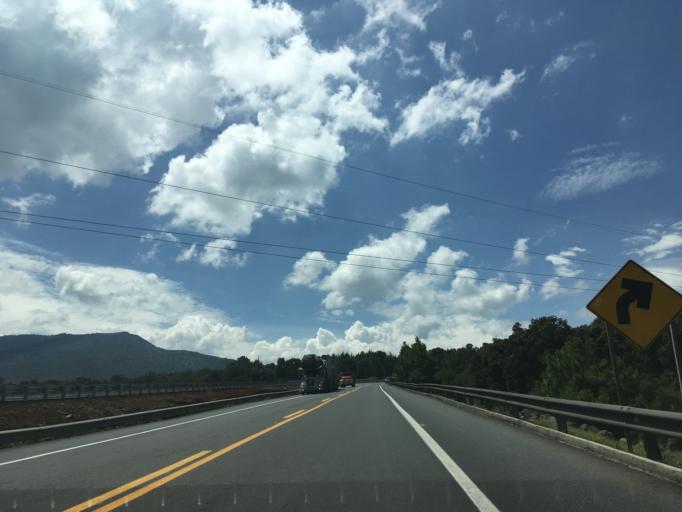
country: MX
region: Michoacan
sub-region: Patzcuaro
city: Colonia Vista Bella (Lomas del Peaje)
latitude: 19.5128
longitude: -101.5737
